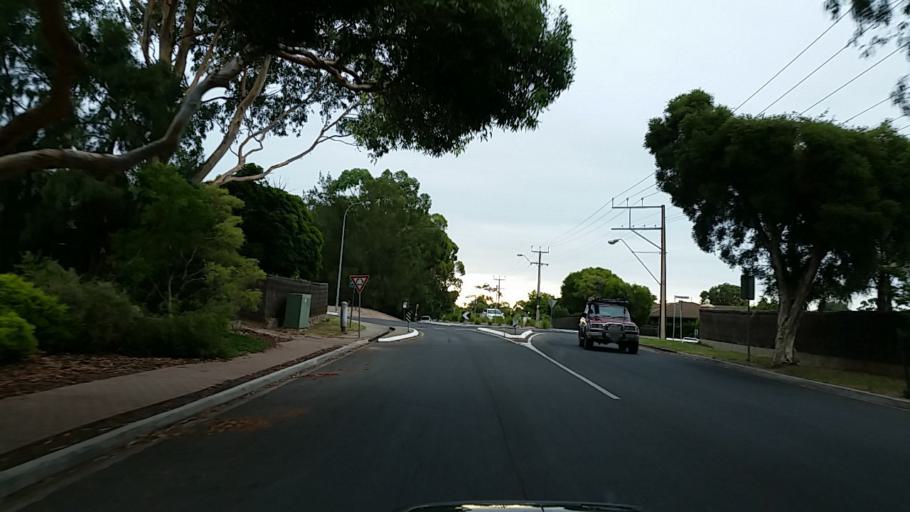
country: AU
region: South Australia
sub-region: Campbelltown
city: Athelstone
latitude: -34.8671
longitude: 138.6943
